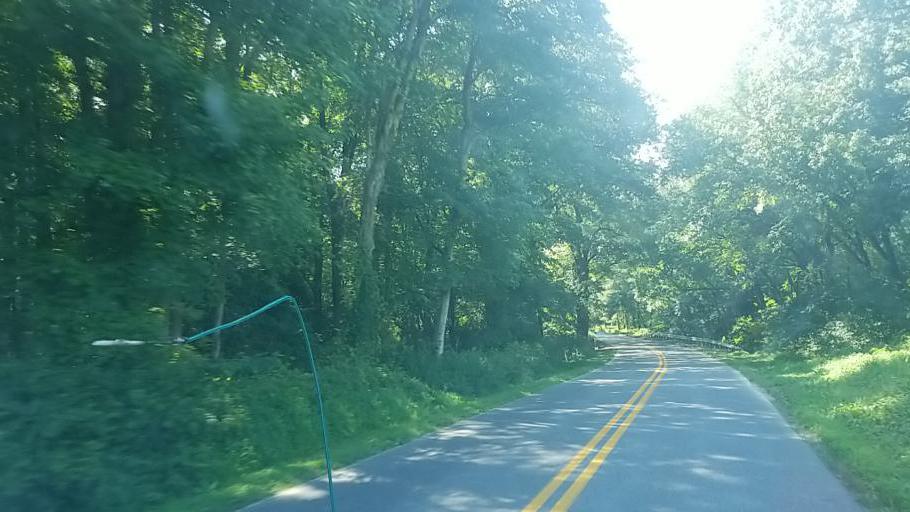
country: US
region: Maryland
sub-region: Somerset County
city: Princess Anne
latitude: 38.2609
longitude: -75.6728
